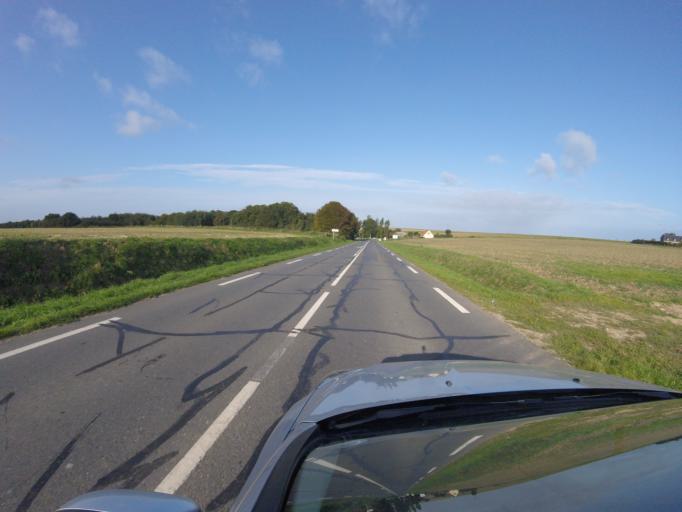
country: FR
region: Haute-Normandie
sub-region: Departement de la Seine-Maritime
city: Fecamp
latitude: 49.7680
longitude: 0.4088
